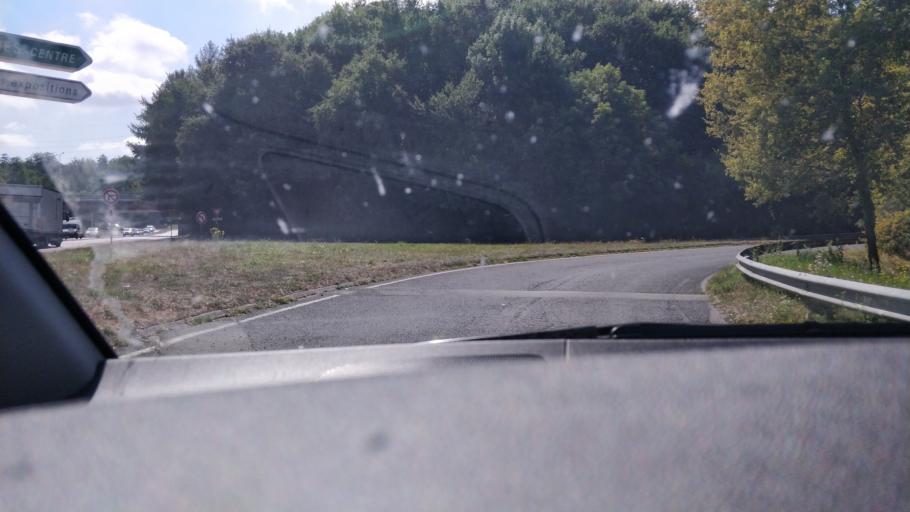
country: FR
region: Limousin
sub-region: Departement de la Haute-Vienne
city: Couzeix
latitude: 45.8638
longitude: 1.2726
